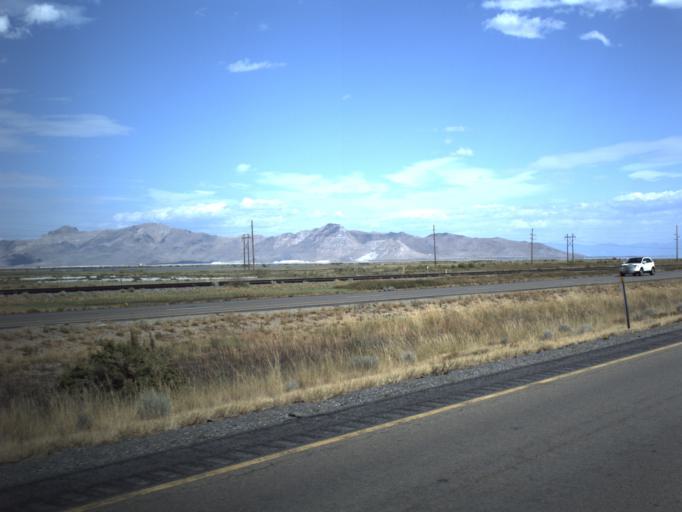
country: US
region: Utah
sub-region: Tooele County
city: Grantsville
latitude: 40.7446
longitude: -112.6409
